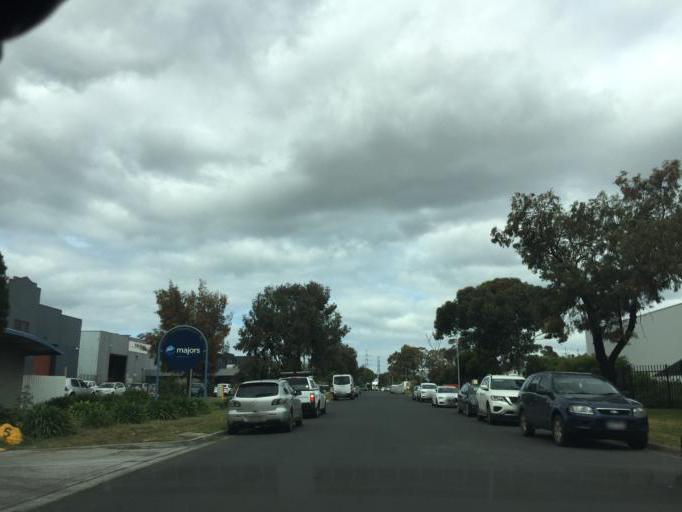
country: AU
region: Victoria
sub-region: Brimbank
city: Brooklyn
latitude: -37.8183
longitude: 144.8555
